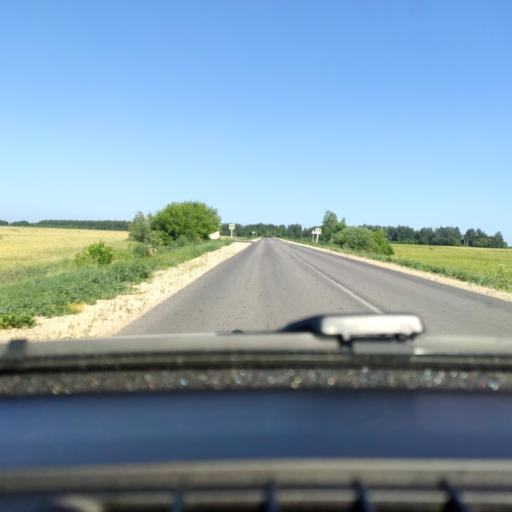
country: RU
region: Voronezj
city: Pereleshinskiy
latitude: 51.6291
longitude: 40.3325
